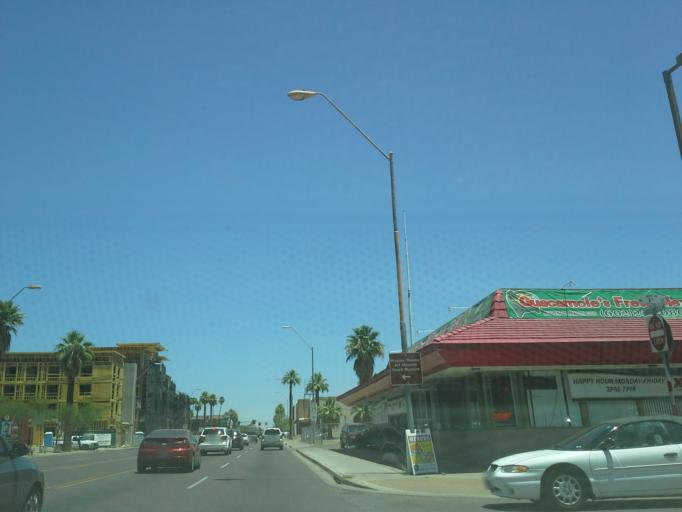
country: US
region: Arizona
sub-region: Maricopa County
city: Phoenix
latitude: 33.4657
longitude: -112.0726
